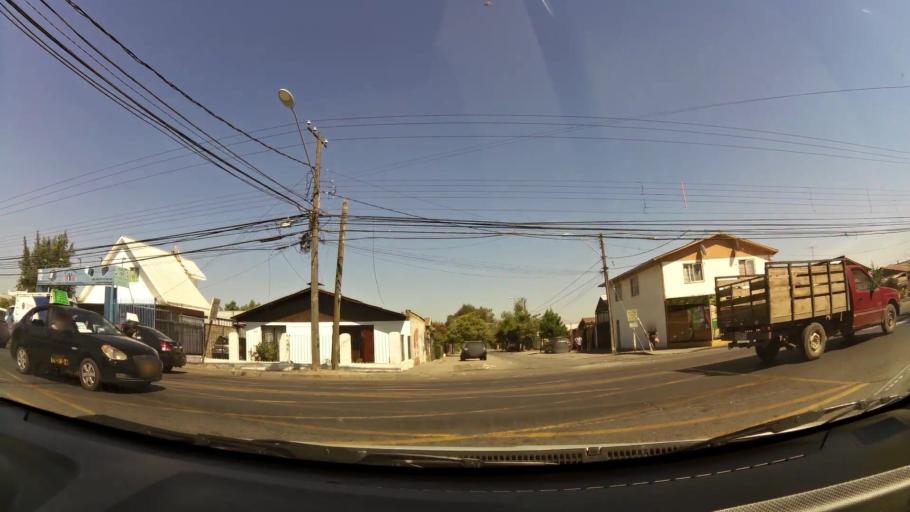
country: CL
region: Maule
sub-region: Provincia de Curico
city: Curico
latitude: -34.9748
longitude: -71.2481
